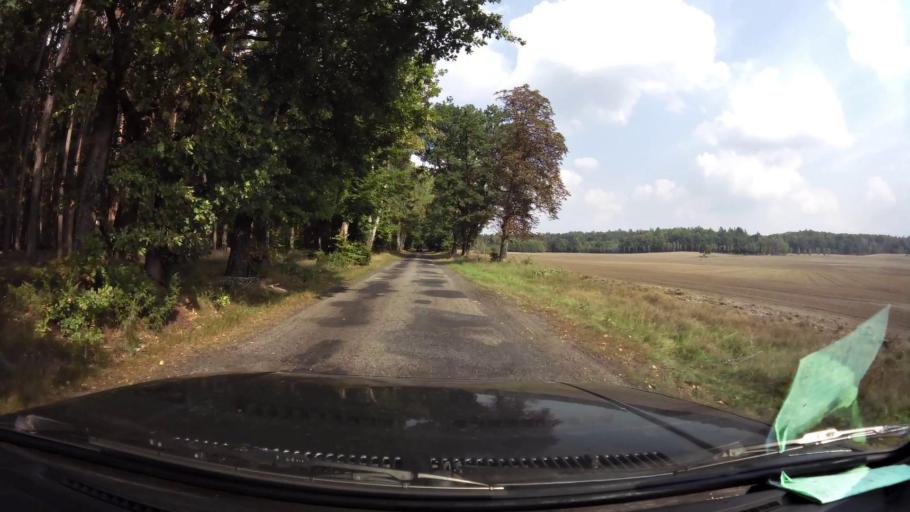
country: PL
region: West Pomeranian Voivodeship
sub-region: Powiat koszalinski
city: Bobolice
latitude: 54.0925
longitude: 16.4862
